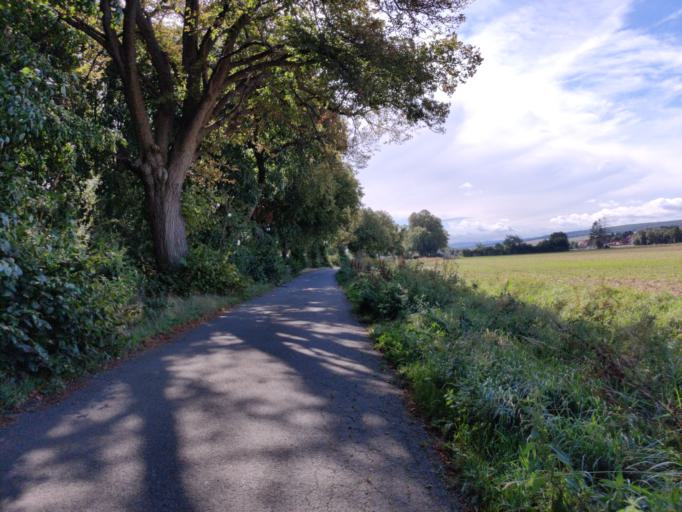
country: DE
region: Lower Saxony
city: Heere
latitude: 52.0707
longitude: 10.2548
